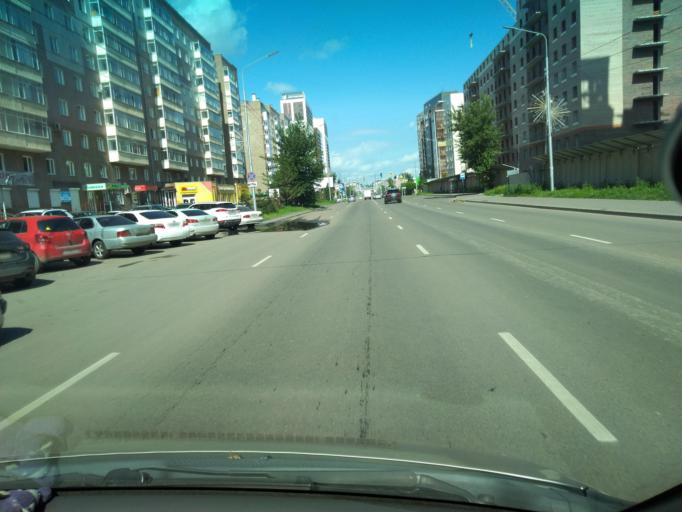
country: RU
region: Krasnoyarskiy
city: Krasnoyarsk
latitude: 56.0447
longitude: 92.9070
